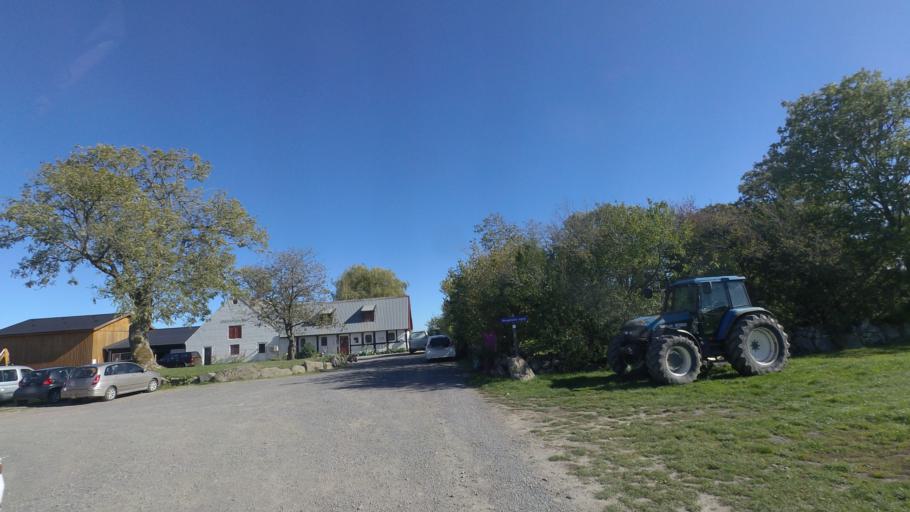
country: DK
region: Capital Region
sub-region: Bornholm Kommune
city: Nexo
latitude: 55.1175
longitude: 15.0594
